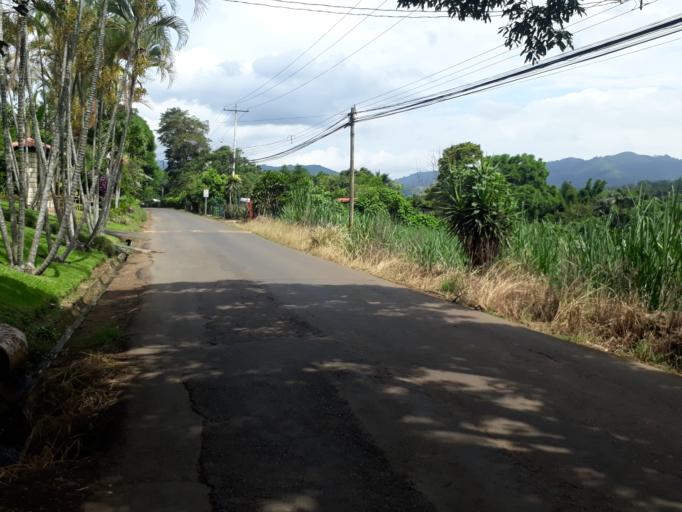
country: CR
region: Alajuela
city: Atenas
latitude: 10.0223
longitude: -84.3388
